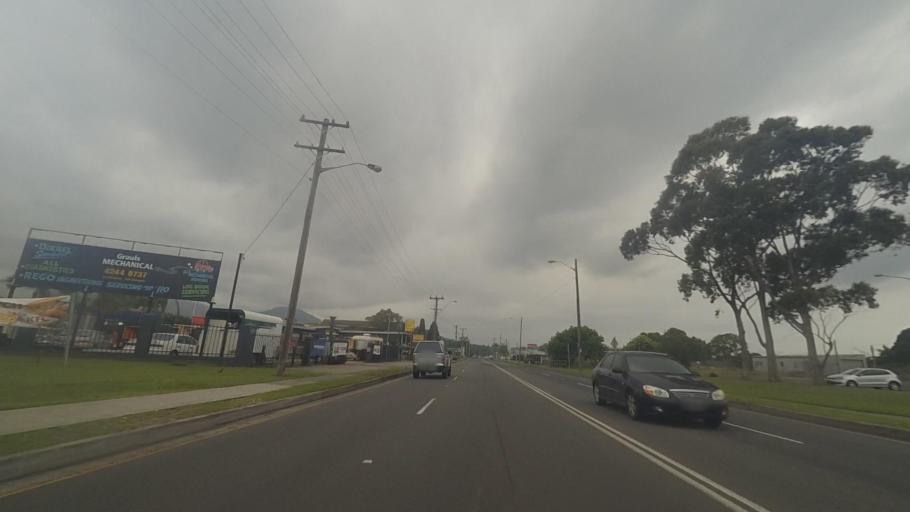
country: AU
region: New South Wales
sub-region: Wollongong
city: Cordeaux Heights
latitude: -34.4538
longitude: 150.8458
